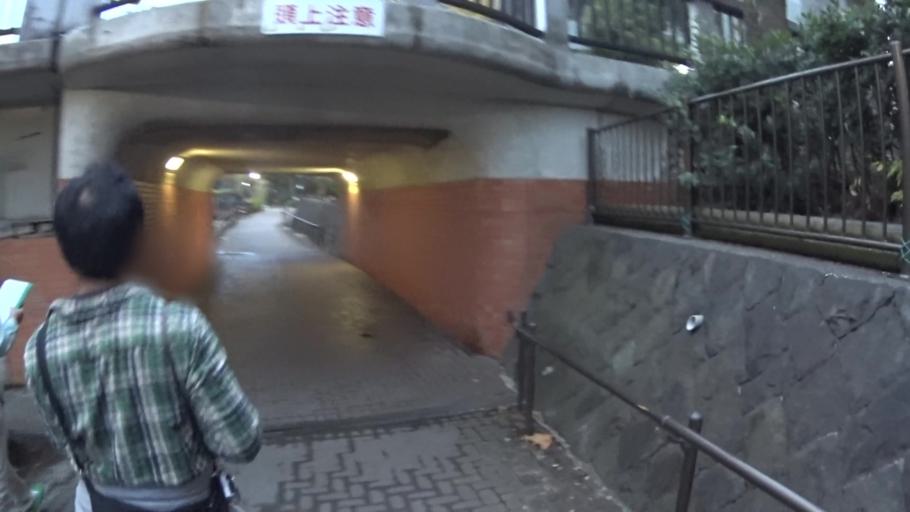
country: JP
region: Tokyo
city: Urayasu
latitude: 35.6787
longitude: 139.8204
